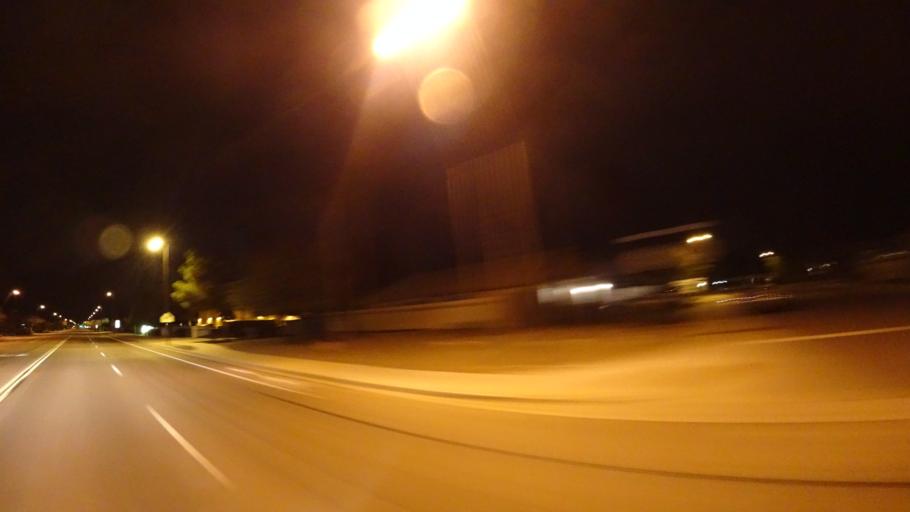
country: US
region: Arizona
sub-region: Maricopa County
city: Gilbert
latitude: 33.3673
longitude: -111.7047
